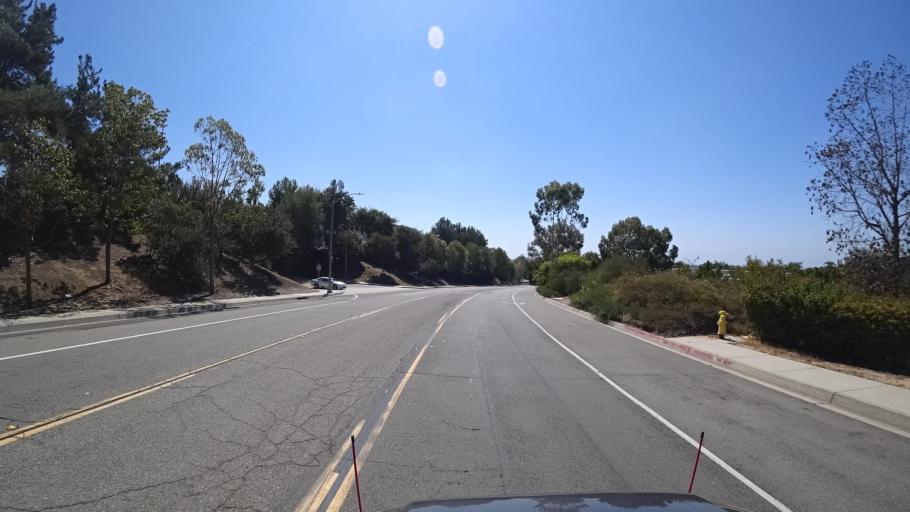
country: US
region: California
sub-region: San Diego County
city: Lake San Marcos
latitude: 33.1362
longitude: -117.2236
